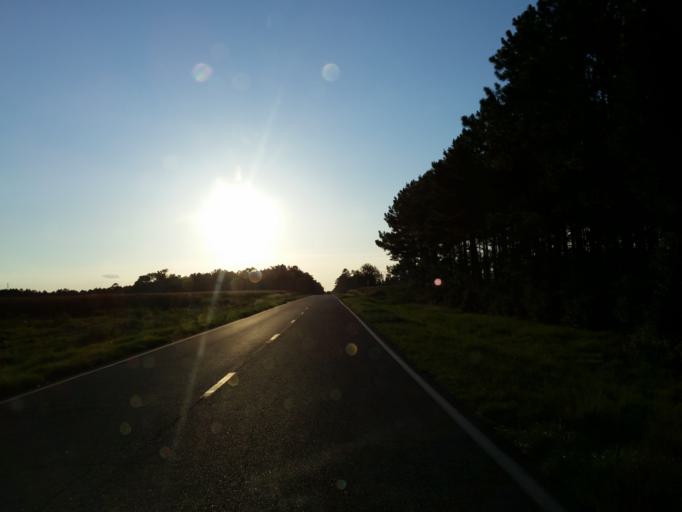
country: US
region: Georgia
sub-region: Lanier County
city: Lakeland
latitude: 31.1651
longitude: -83.0919
